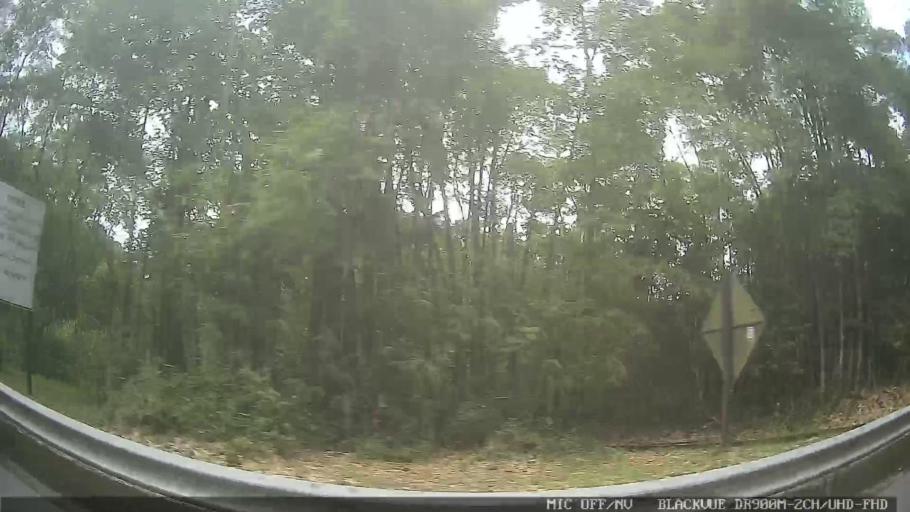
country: BR
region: Sao Paulo
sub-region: Caraguatatuba
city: Caraguatatuba
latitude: -23.5919
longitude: -45.4541
